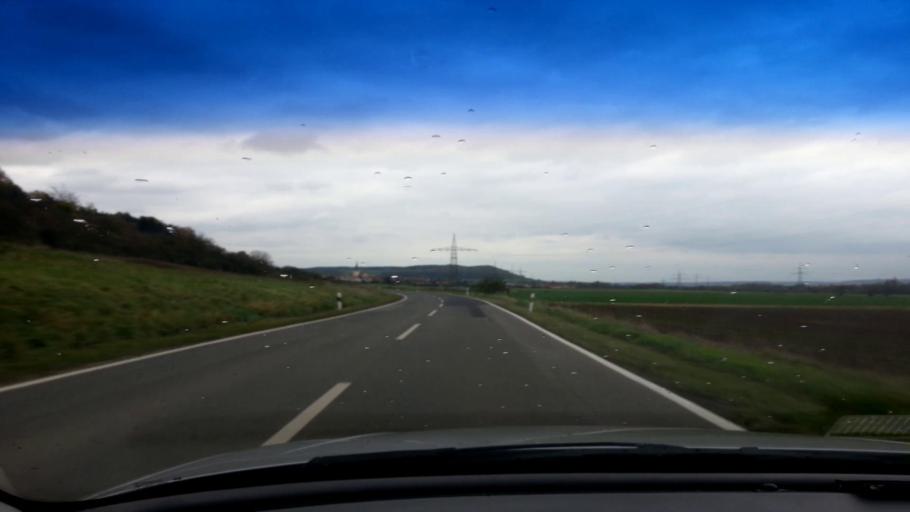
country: DE
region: Bavaria
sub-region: Regierungsbezirk Unterfranken
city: Stettfeld
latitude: 49.9766
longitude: 10.7057
